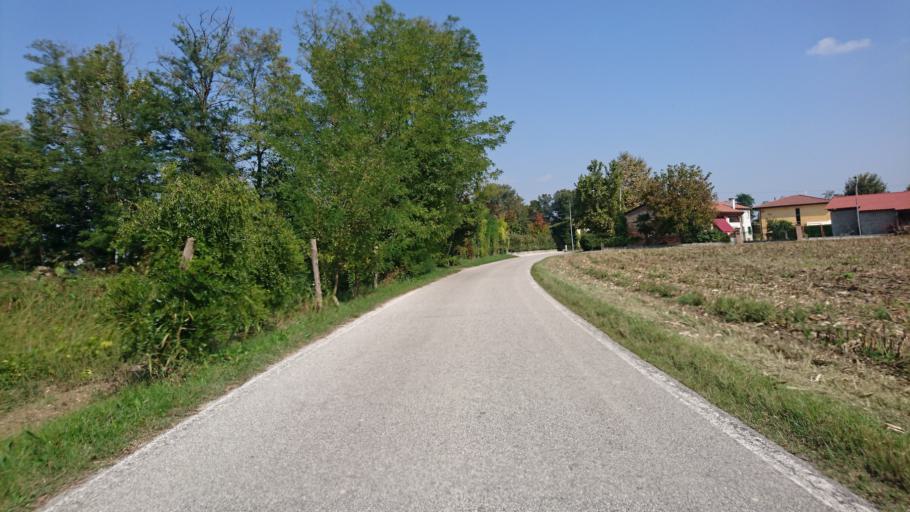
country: IT
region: Veneto
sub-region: Provincia di Padova
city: San Giorgio in Bosco
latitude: 45.5711
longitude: 11.7908
